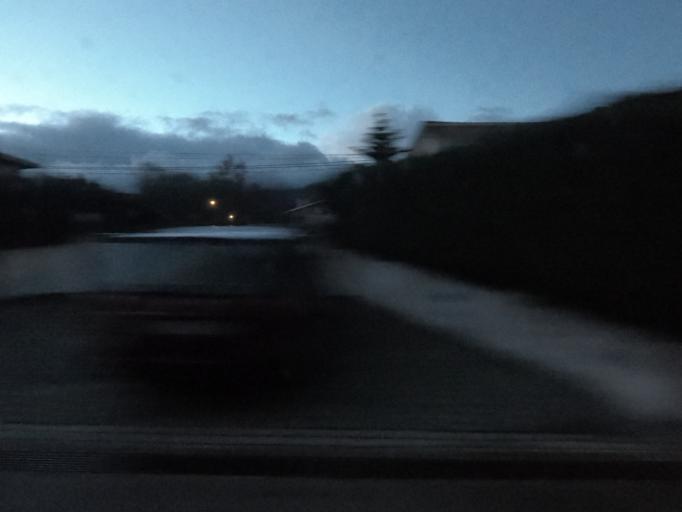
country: PT
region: Vila Real
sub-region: Vila Real
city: Vila Real
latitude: 41.3477
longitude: -7.7221
